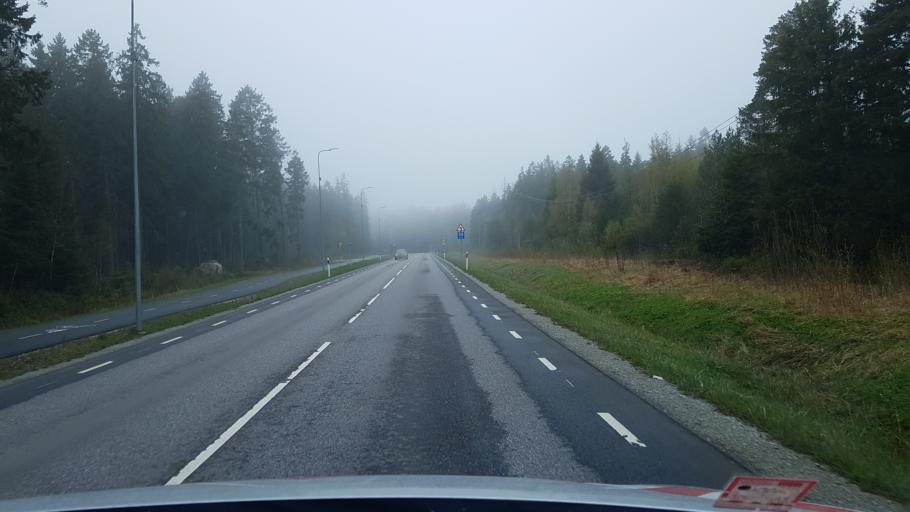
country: EE
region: Harju
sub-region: Viimsi vald
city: Viimsi
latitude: 59.5193
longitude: 24.8977
